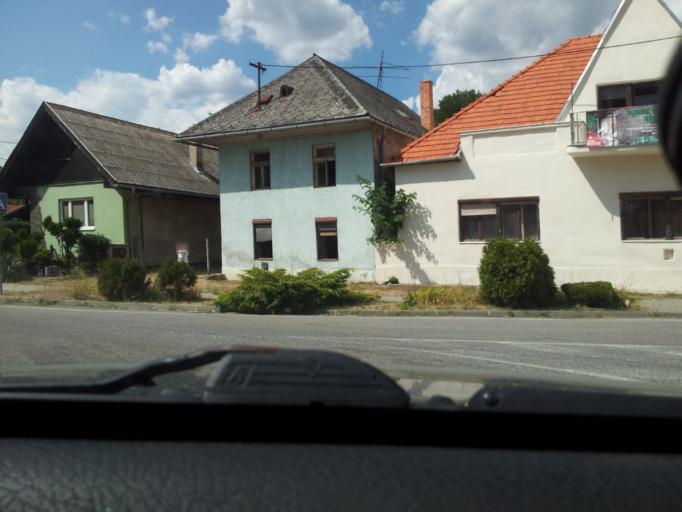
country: SK
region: Nitriansky
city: Tlmace
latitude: 48.3455
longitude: 18.5589
